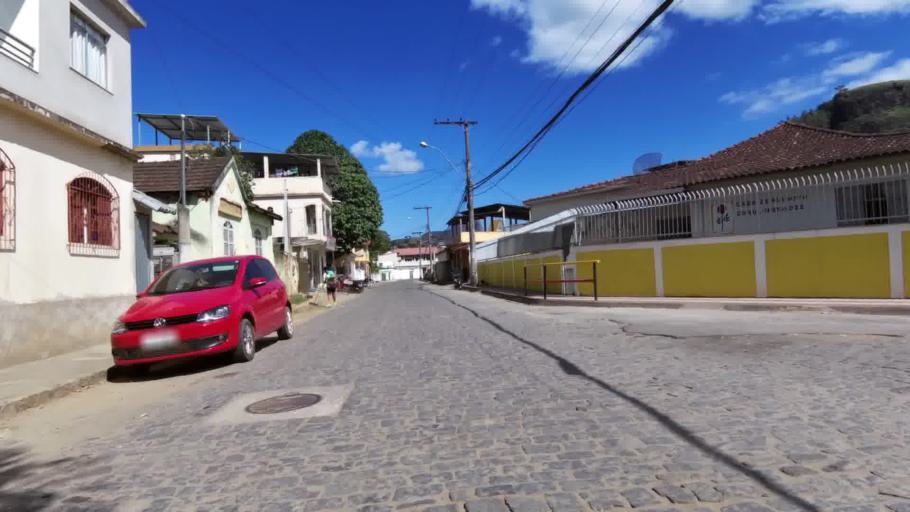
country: BR
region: Espirito Santo
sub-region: Rio Novo Do Sul
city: Rio Novo do Sul
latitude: -20.8649
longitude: -40.9345
